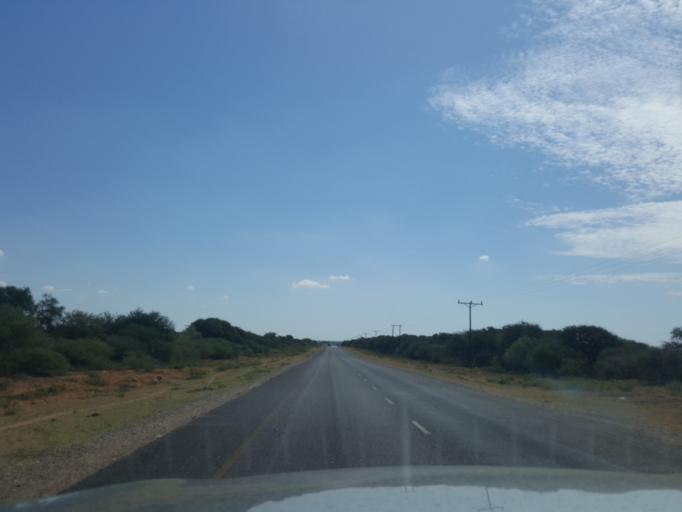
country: BW
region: Kweneng
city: Letlhakeng
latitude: -24.1202
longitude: 25.0722
